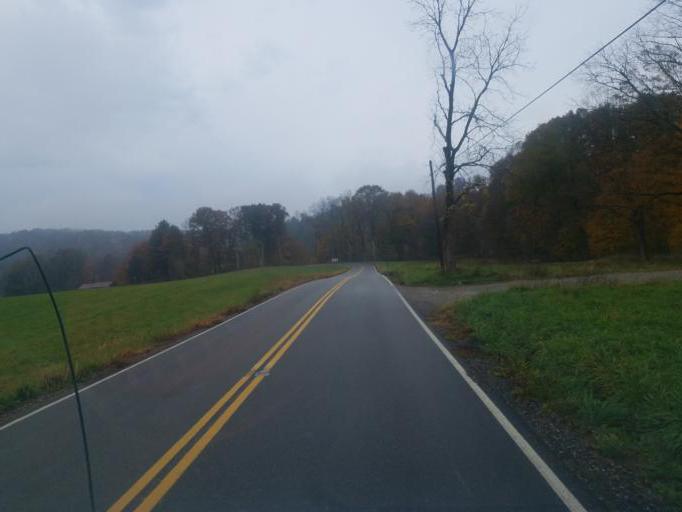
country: US
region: Ohio
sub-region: Morgan County
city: McConnelsville
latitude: 39.5583
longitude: -81.7891
